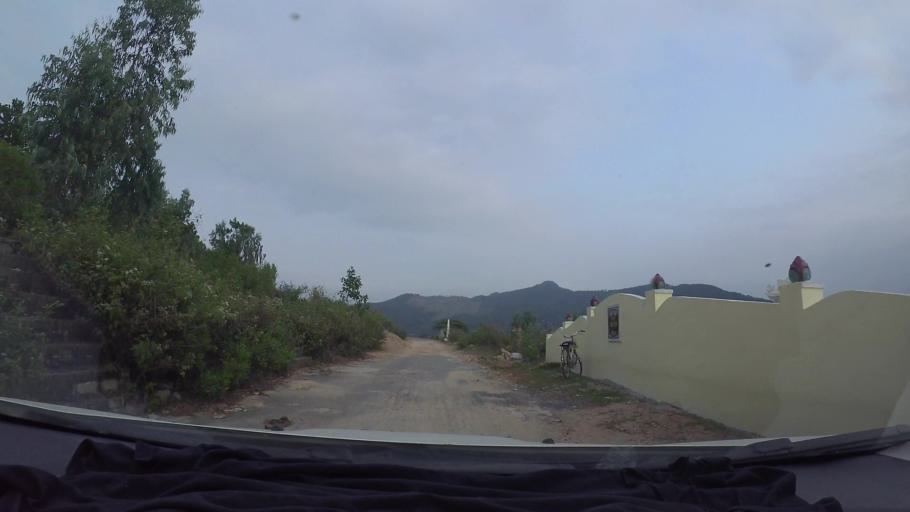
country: VN
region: Da Nang
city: Lien Chieu
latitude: 16.0626
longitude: 108.1120
